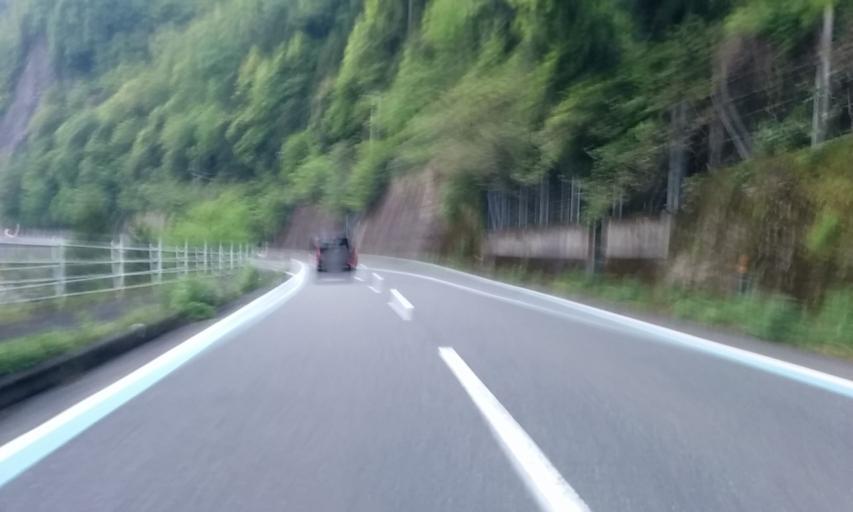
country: JP
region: Ehime
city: Saijo
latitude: 33.8560
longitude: 133.1974
